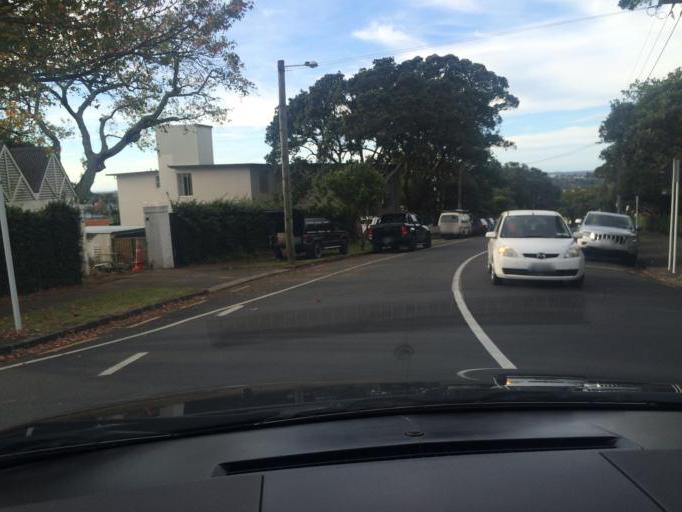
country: NZ
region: Auckland
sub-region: Auckland
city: Auckland
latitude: -36.8782
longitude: 174.7923
